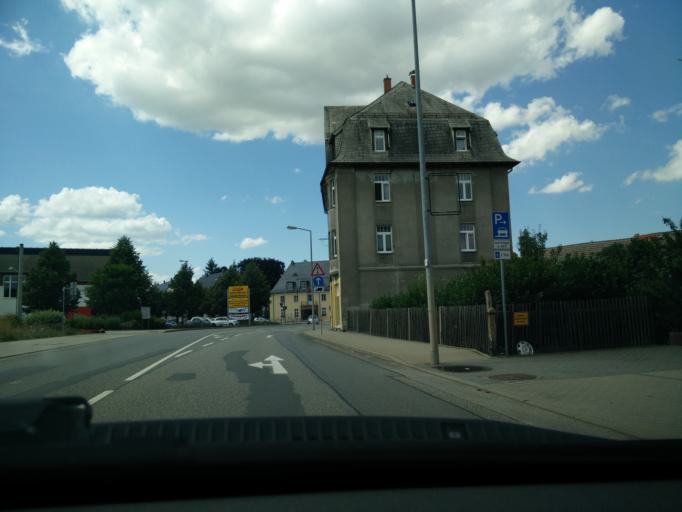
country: DE
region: Saxony
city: Hartmannsdorf
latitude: 50.8868
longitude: 12.7994
